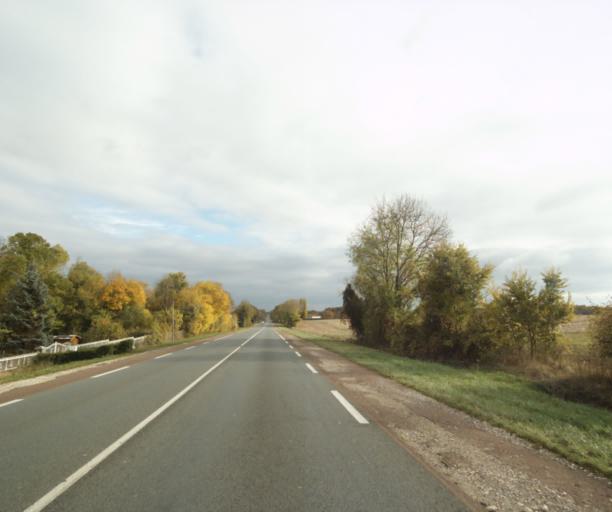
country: FR
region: Poitou-Charentes
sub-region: Departement de la Charente-Maritime
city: Saint-Georges-des-Coteaux
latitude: 45.7671
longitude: -0.6801
